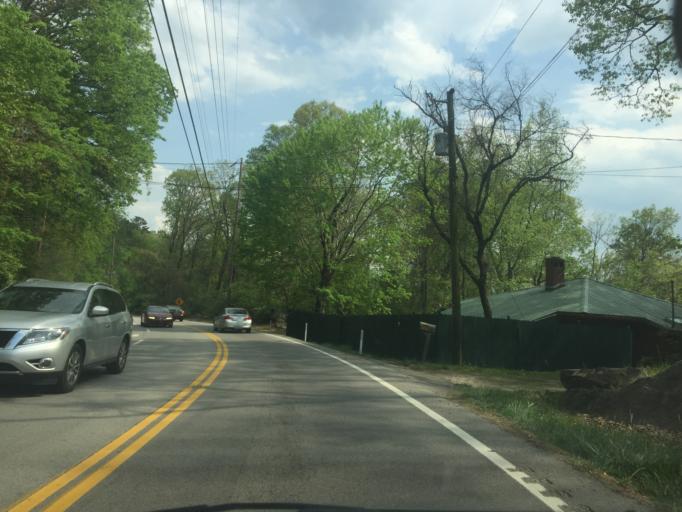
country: US
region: Tennessee
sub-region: Hamilton County
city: Signal Mountain
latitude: 35.1088
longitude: -85.3503
